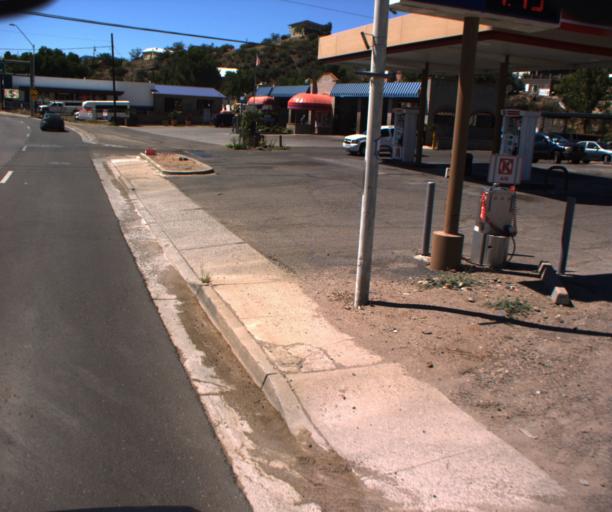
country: US
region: Arizona
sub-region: Gila County
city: Globe
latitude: 33.4029
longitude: -110.7926
